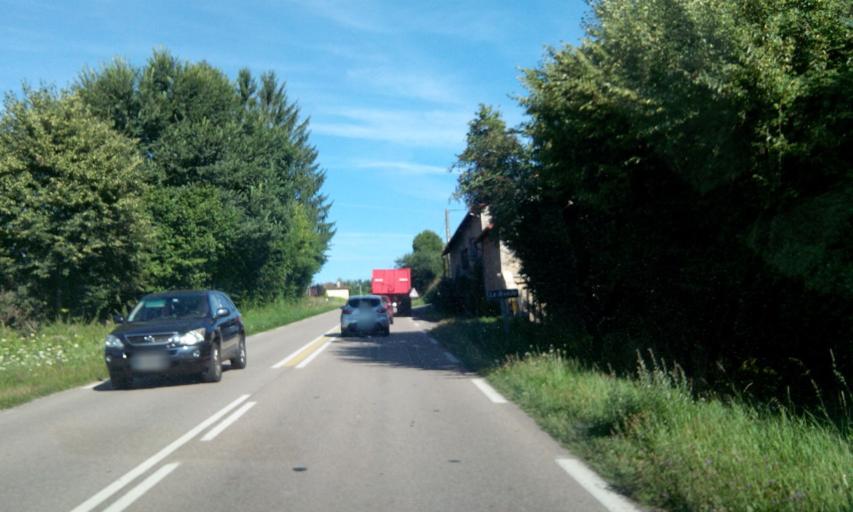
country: FR
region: Limousin
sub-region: Departement de la Haute-Vienne
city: Saint-Leonard-de-Noblat
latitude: 45.8451
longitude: 1.4593
